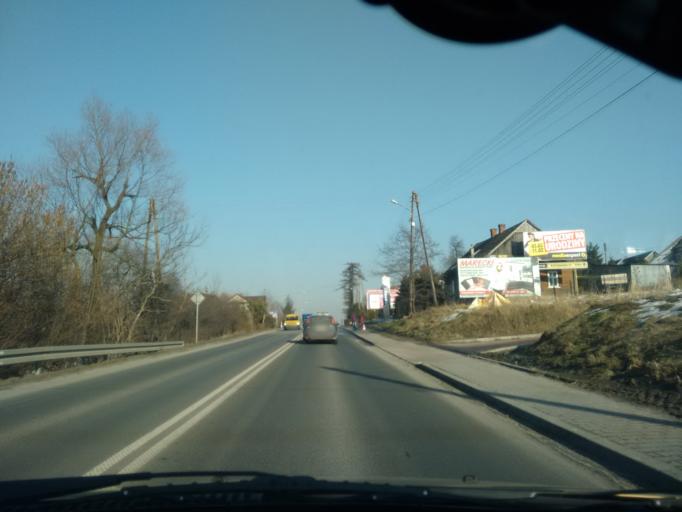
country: PL
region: Lesser Poland Voivodeship
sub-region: Powiat wadowicki
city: Chocznia
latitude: 49.8810
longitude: 19.4691
